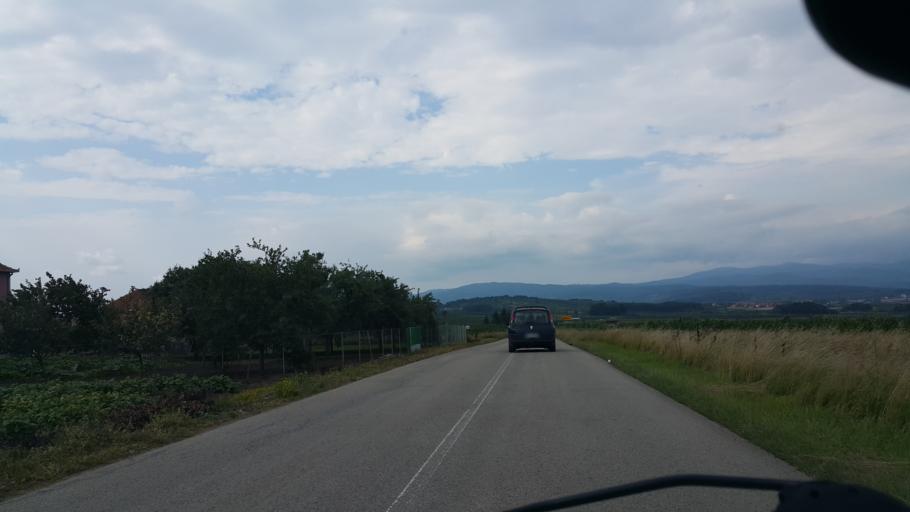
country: RS
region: Central Serbia
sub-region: Toplicki Okrug
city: Blace
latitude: 43.2664
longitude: 21.2732
